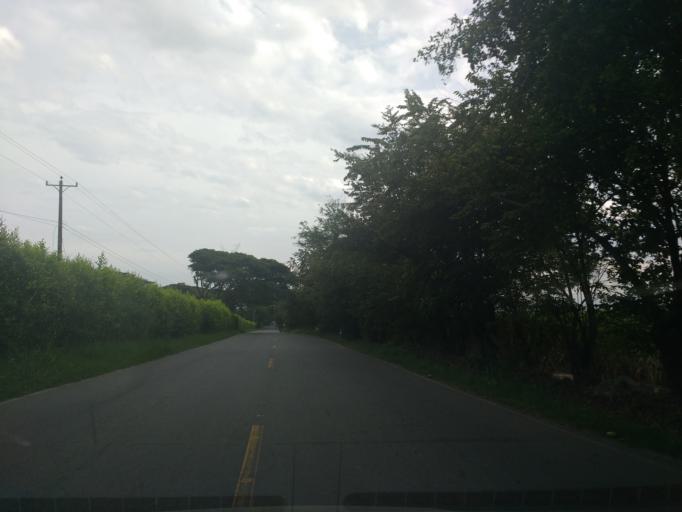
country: CO
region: Valle del Cauca
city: Florida
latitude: 3.3040
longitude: -76.2329
